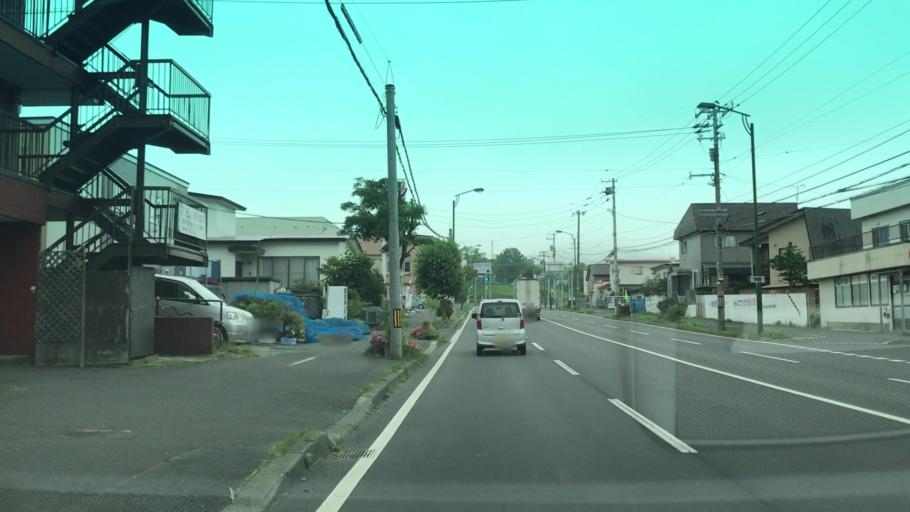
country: JP
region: Hokkaido
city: Muroran
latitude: 42.3640
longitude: 141.0379
